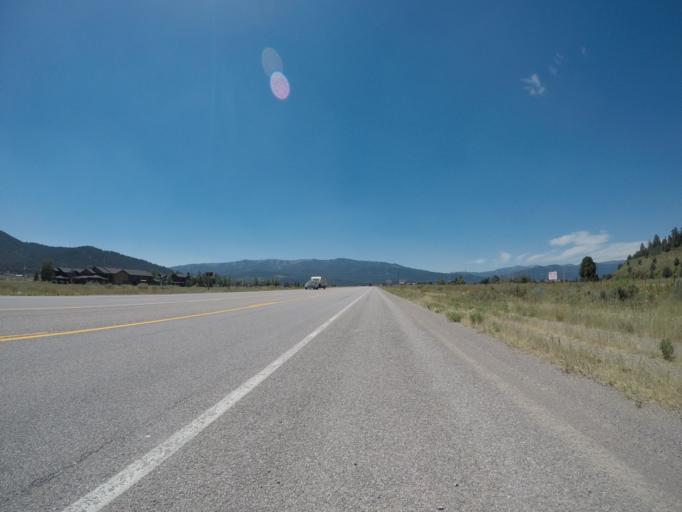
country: US
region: Wyoming
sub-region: Teton County
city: Hoback
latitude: 43.1738
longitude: -111.0112
